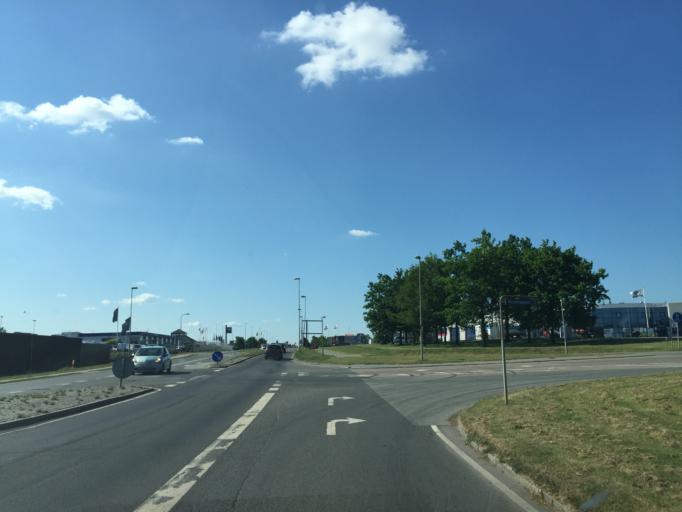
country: DK
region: South Denmark
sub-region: Odense Kommune
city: Hojby
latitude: 55.3491
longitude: 10.4121
